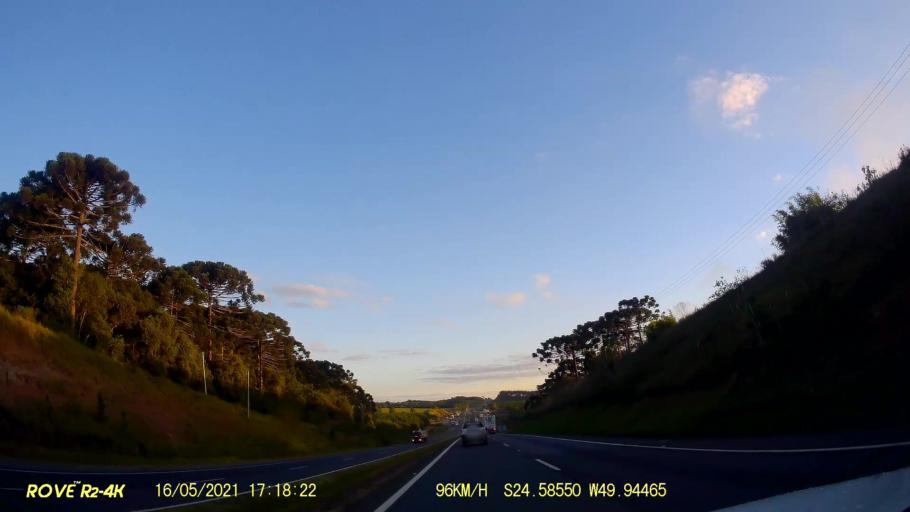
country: BR
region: Parana
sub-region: Pirai Do Sul
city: Pirai do Sul
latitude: -24.5859
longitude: -49.9448
